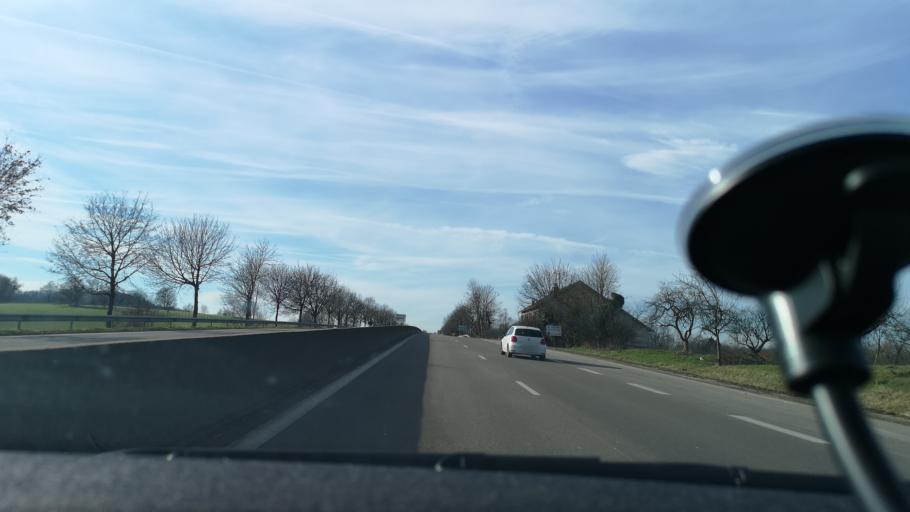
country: FR
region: Franche-Comte
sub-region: Departement du Doubs
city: Grandfontaine
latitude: 47.2070
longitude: 5.8986
